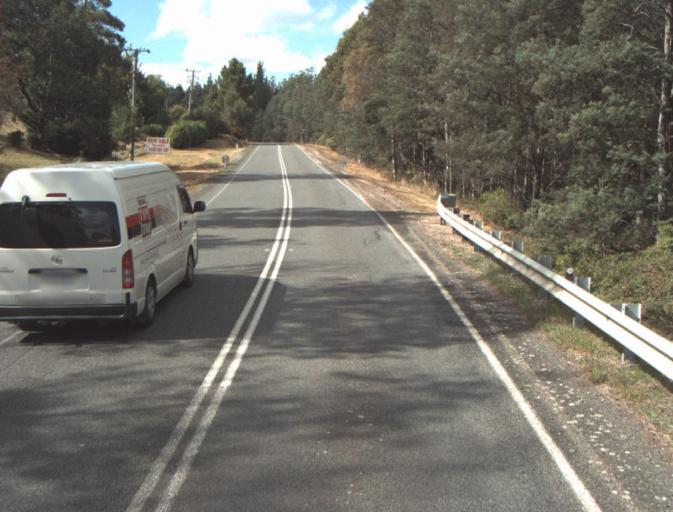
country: AU
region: Tasmania
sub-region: Launceston
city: Mayfield
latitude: -41.2686
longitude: 147.2138
